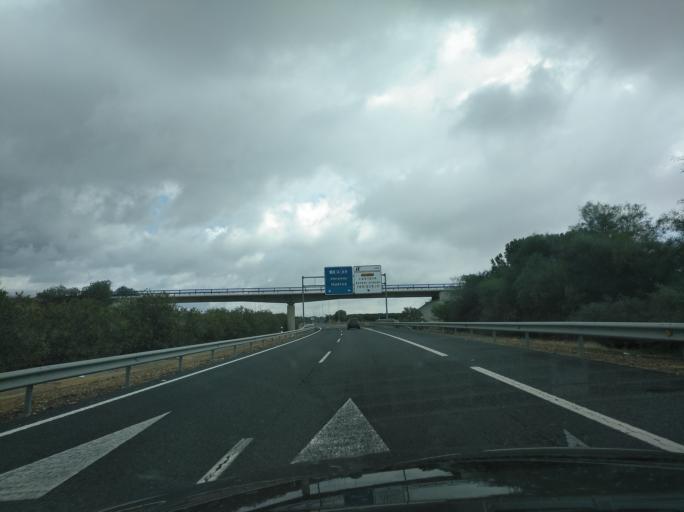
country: ES
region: Andalusia
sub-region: Provincia de Huelva
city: Cartaya
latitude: 37.3302
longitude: -7.1653
